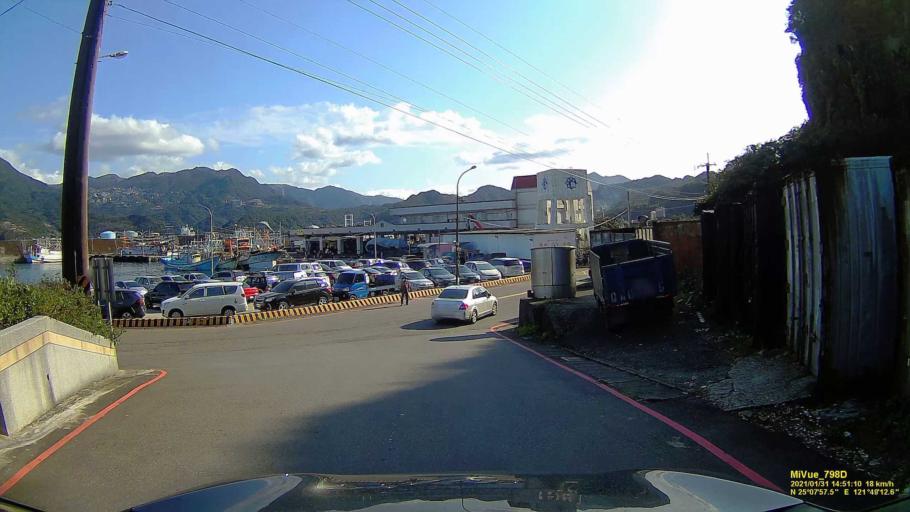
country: TW
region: Taiwan
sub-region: Keelung
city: Keelung
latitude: 25.1326
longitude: 121.8202
